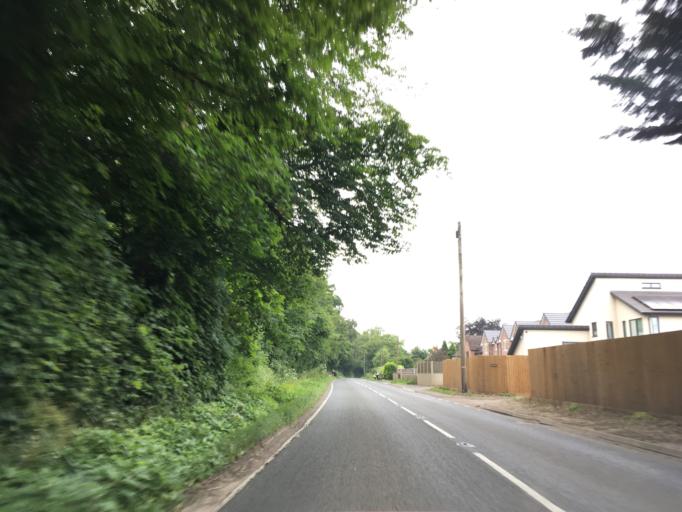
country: GB
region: England
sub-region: Gloucestershire
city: Stonehouse
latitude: 51.7684
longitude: -2.3556
